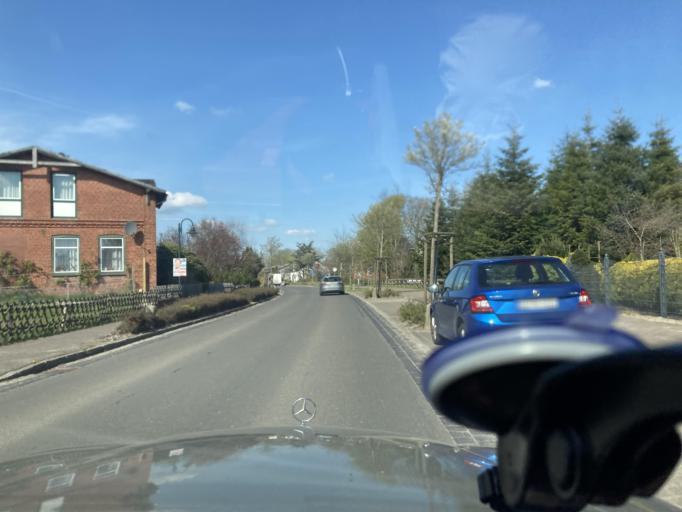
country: DE
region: Schleswig-Holstein
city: Lehe
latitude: 54.3391
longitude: 9.0243
